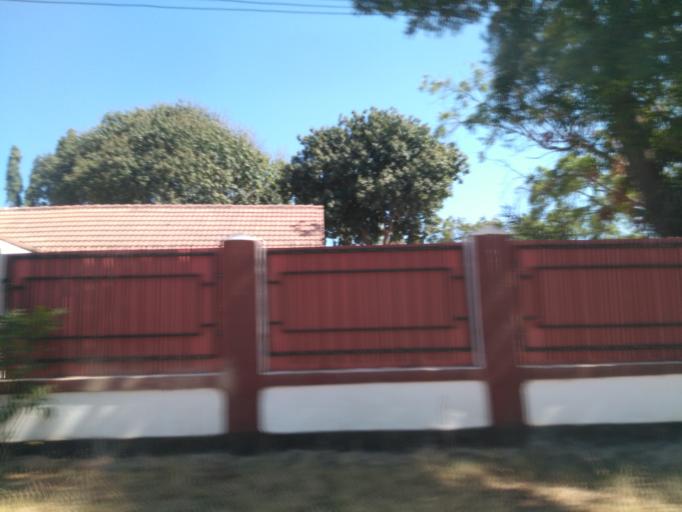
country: TZ
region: Dodoma
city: Dodoma
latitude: -6.1660
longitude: 35.7533
